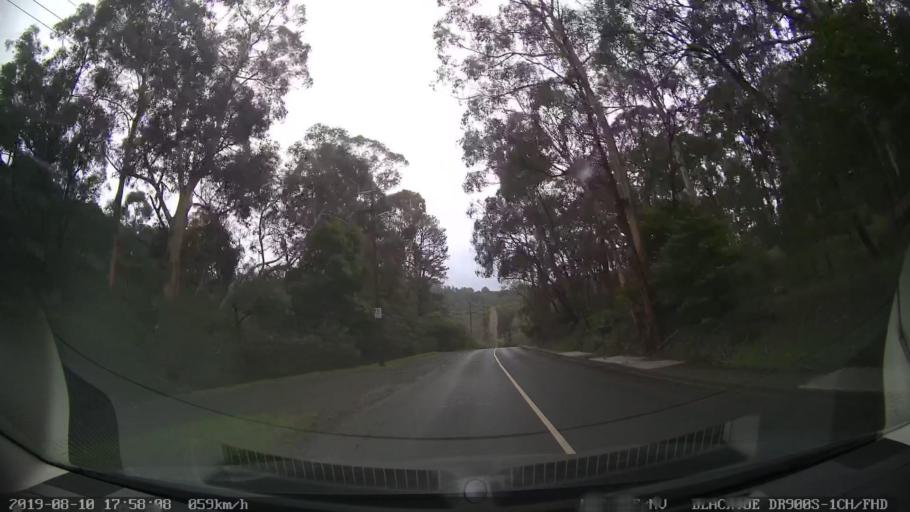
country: AU
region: Victoria
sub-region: Yarra Ranges
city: Tremont
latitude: -37.8975
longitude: 145.3338
